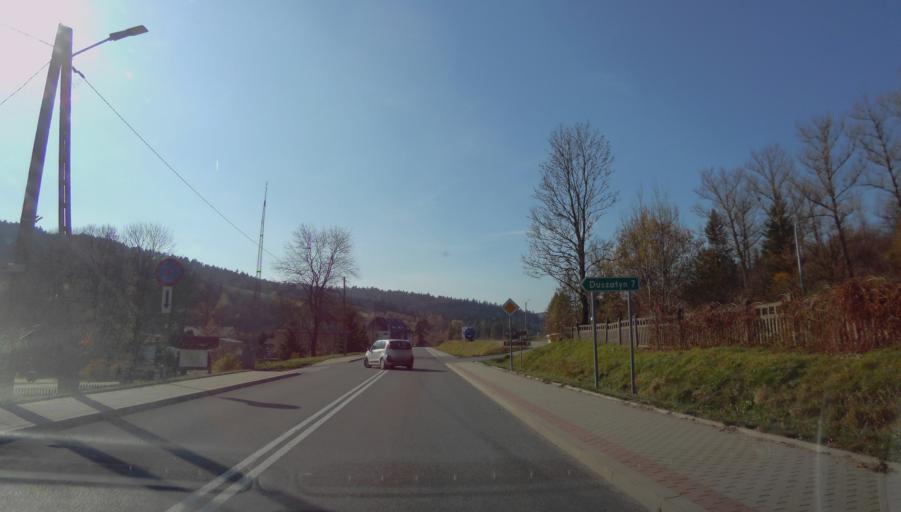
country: PL
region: Subcarpathian Voivodeship
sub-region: Powiat sanocki
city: Komancza
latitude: 49.3383
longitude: 22.0726
